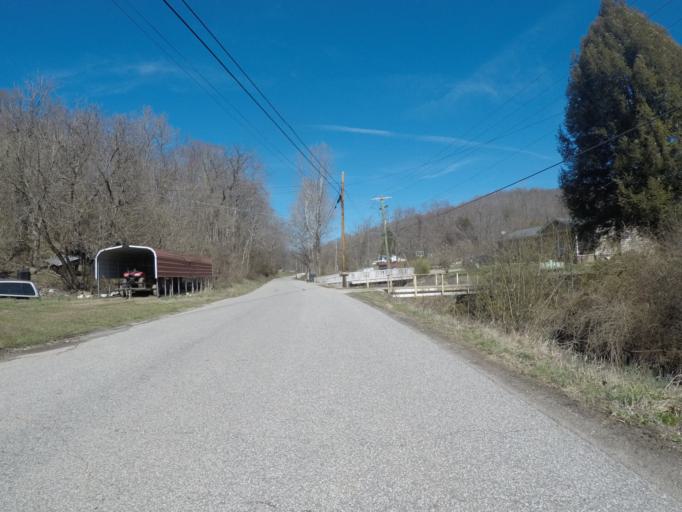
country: US
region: Ohio
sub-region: Lawrence County
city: Burlington
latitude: 38.4470
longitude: -82.5039
